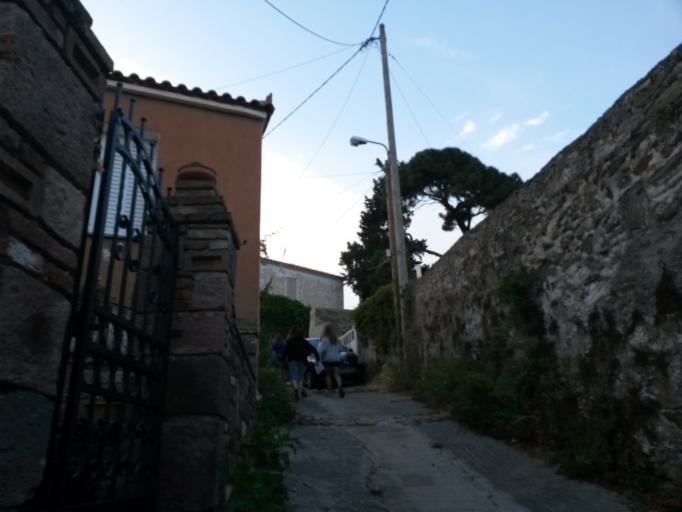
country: GR
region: North Aegean
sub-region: Nomos Lesvou
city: Pamfylla
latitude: 39.1745
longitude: 26.4984
